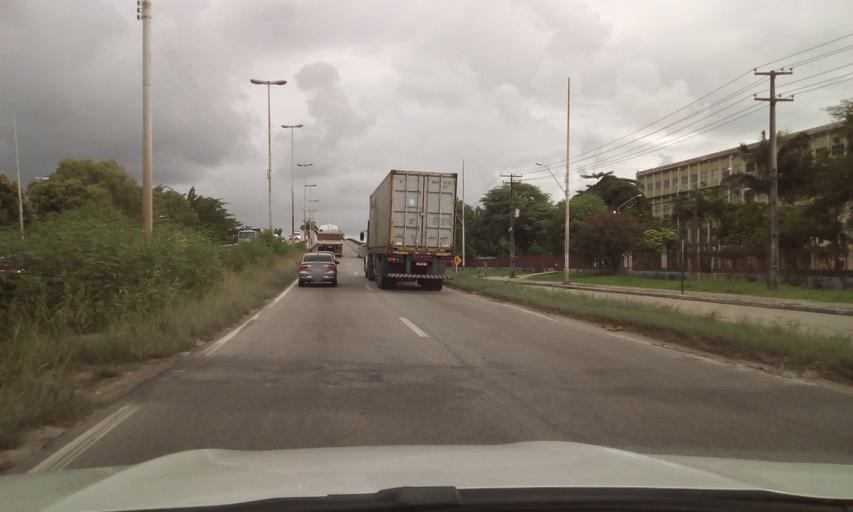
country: BR
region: Pernambuco
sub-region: Recife
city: Recife
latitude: -8.0499
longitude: -34.9457
